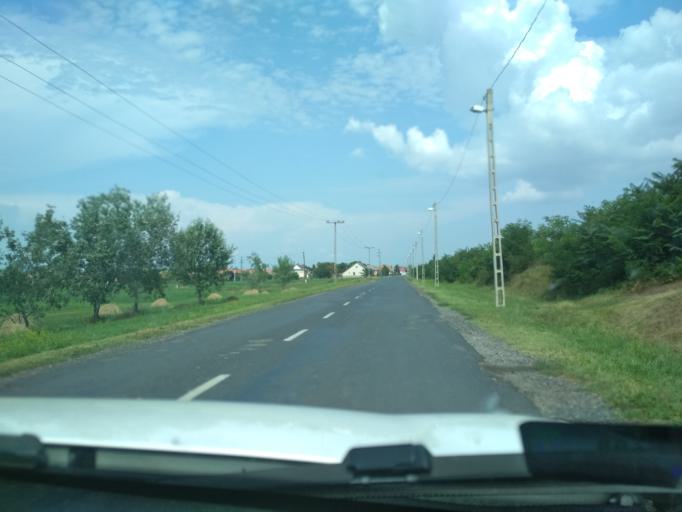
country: HU
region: Jasz-Nagykun-Szolnok
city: Abadszalok
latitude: 47.4708
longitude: 20.5954
